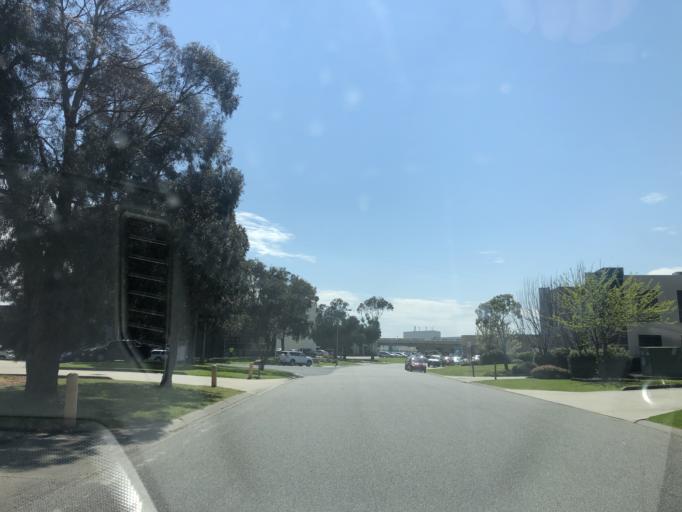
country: AU
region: Victoria
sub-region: Casey
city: Hampton Park
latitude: -38.0318
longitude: 145.2404
